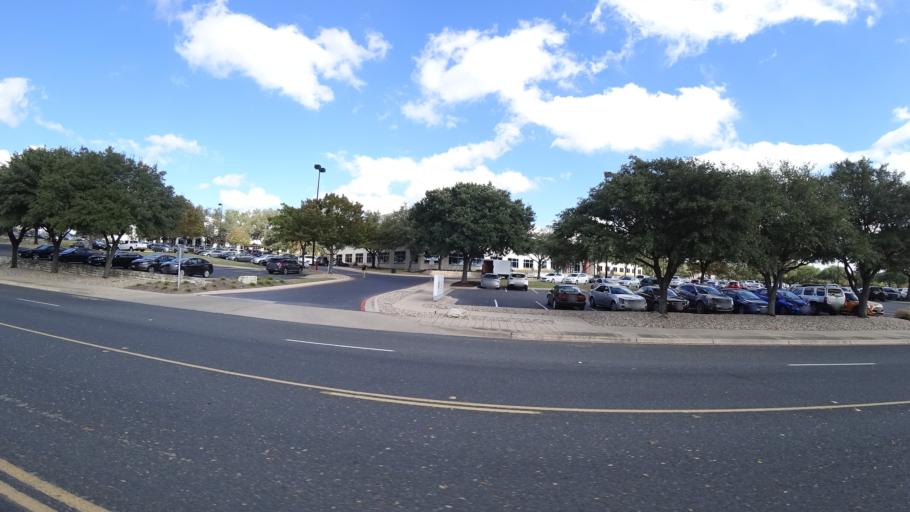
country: US
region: Texas
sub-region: Williamson County
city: Jollyville
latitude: 30.4312
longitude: -97.7376
